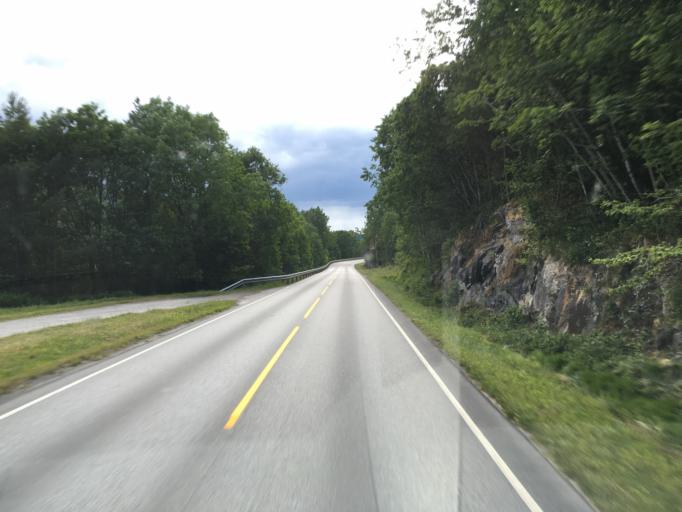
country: NO
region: More og Romsdal
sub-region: Tingvoll
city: Tingvoll
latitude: 62.9743
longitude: 8.0597
